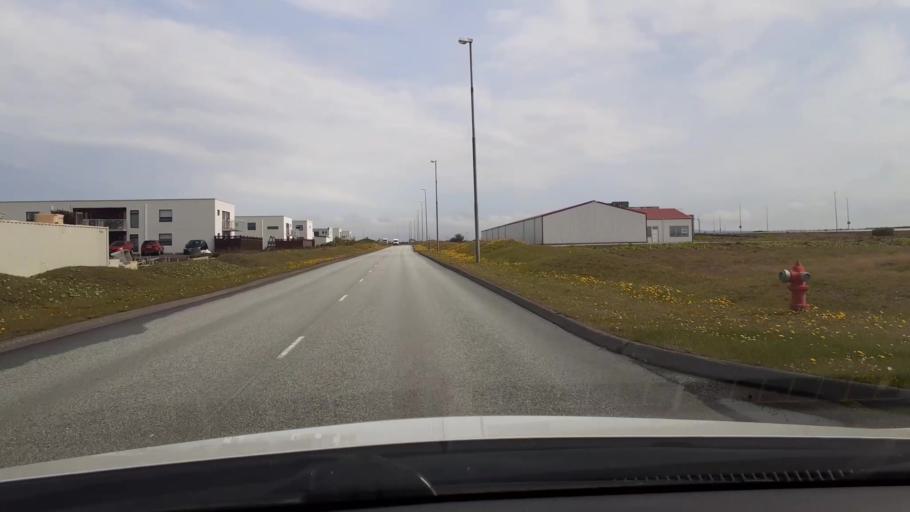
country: IS
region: Southern Peninsula
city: Reykjanesbaer
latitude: 63.9714
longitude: -22.5229
